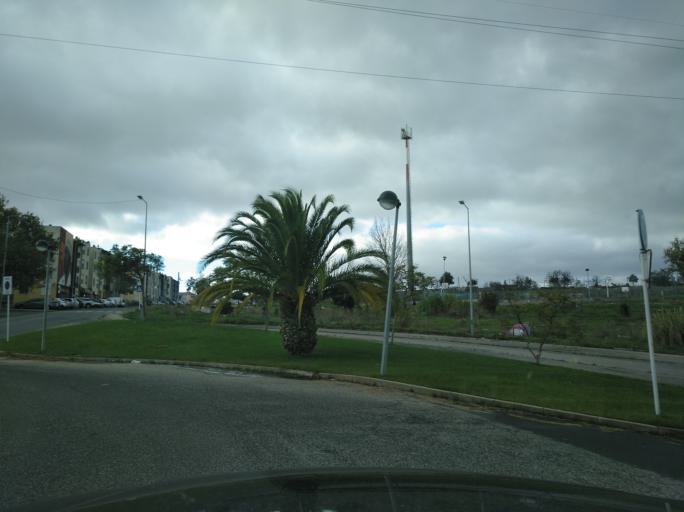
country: PT
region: Lisbon
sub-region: Loures
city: Sacavem
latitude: 38.8006
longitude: -9.1145
